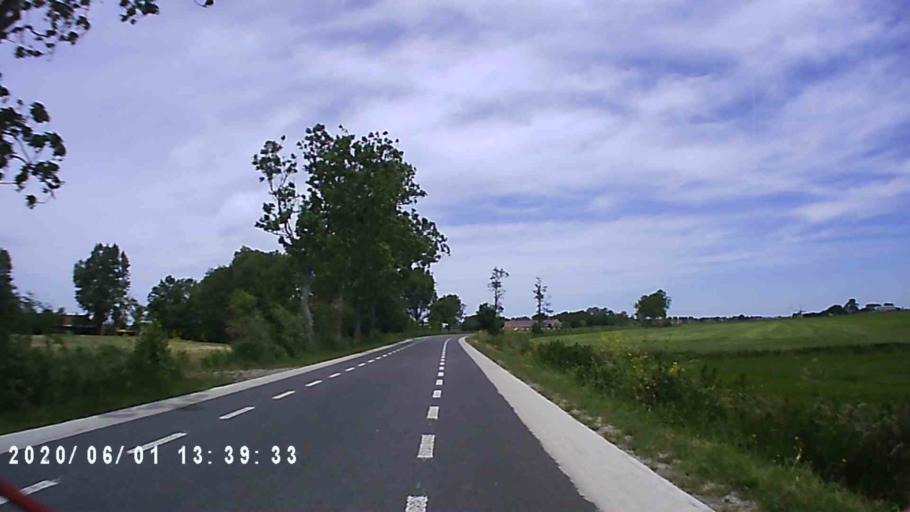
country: NL
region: Friesland
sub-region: Gemeente Littenseradiel
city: Wommels
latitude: 53.0868
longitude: 5.5999
